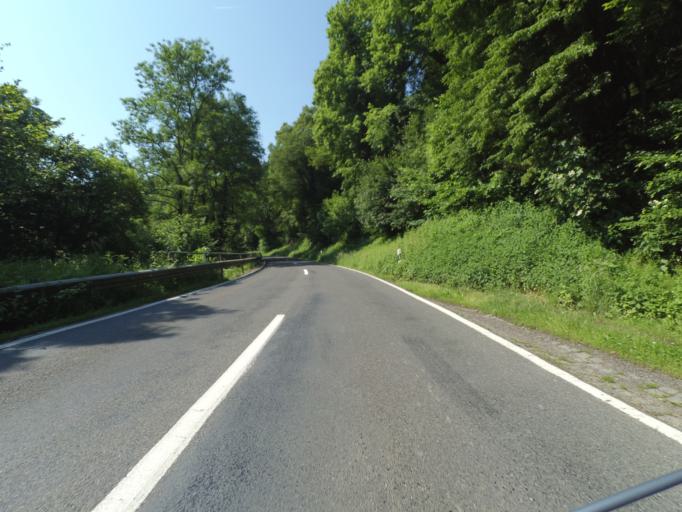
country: DE
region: Rheinland-Pfalz
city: Pommern
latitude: 50.1433
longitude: 7.2751
